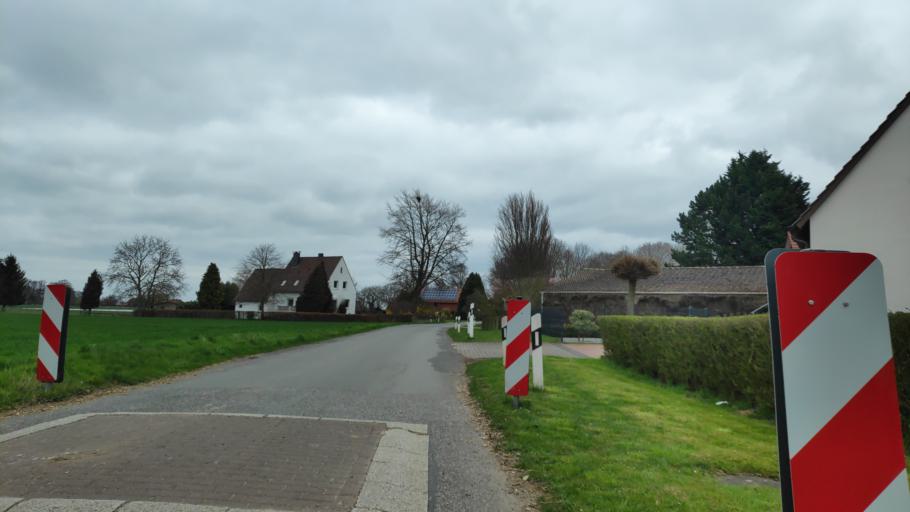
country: DE
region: North Rhine-Westphalia
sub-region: Regierungsbezirk Detmold
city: Minden
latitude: 52.3240
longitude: 8.8531
